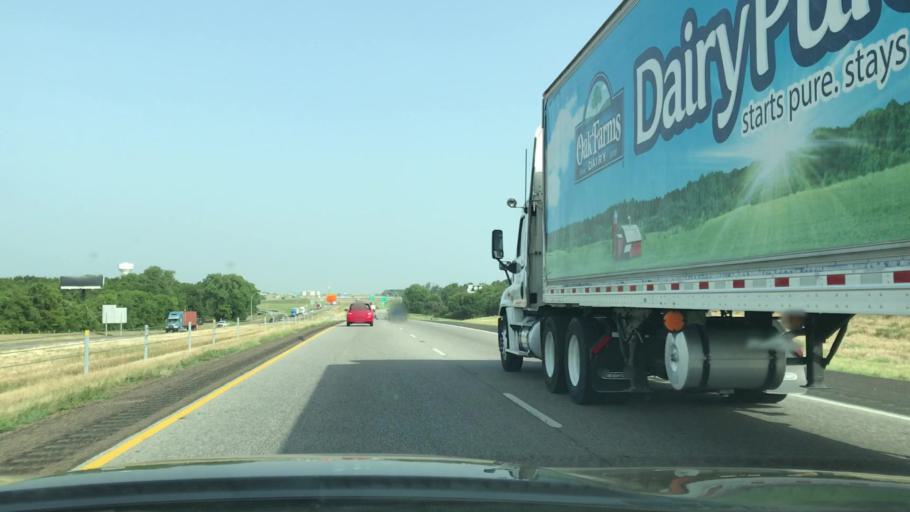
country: US
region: Texas
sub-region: Kaufman County
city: Terrell
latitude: 32.7088
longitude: -96.2917
